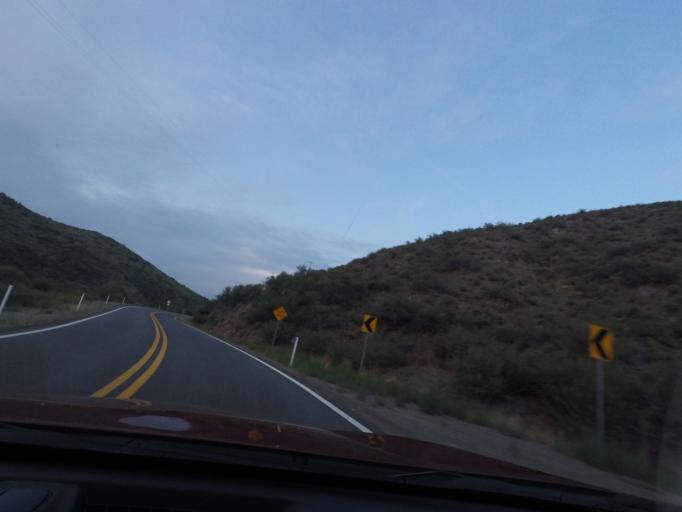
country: US
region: Arizona
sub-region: Yavapai County
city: Prescott
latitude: 34.4214
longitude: -112.7006
